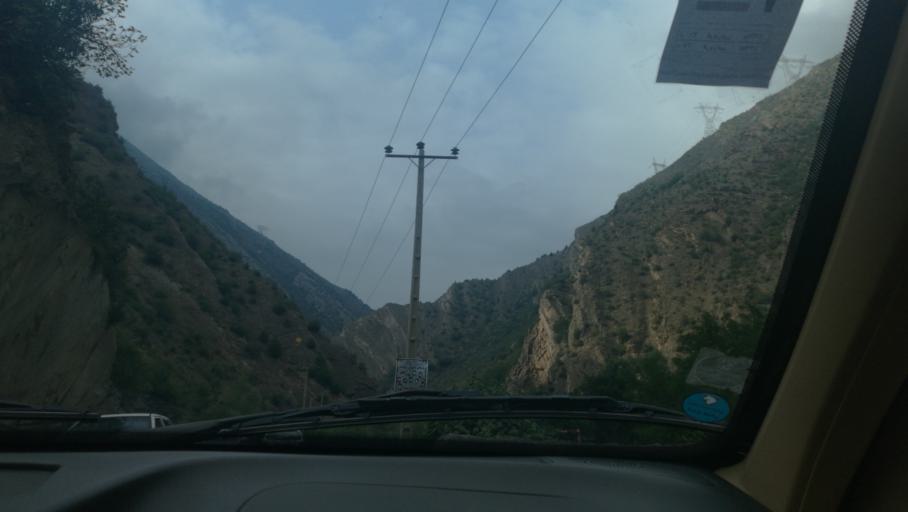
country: IR
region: Mazandaran
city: Chalus
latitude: 36.3094
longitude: 51.2477
